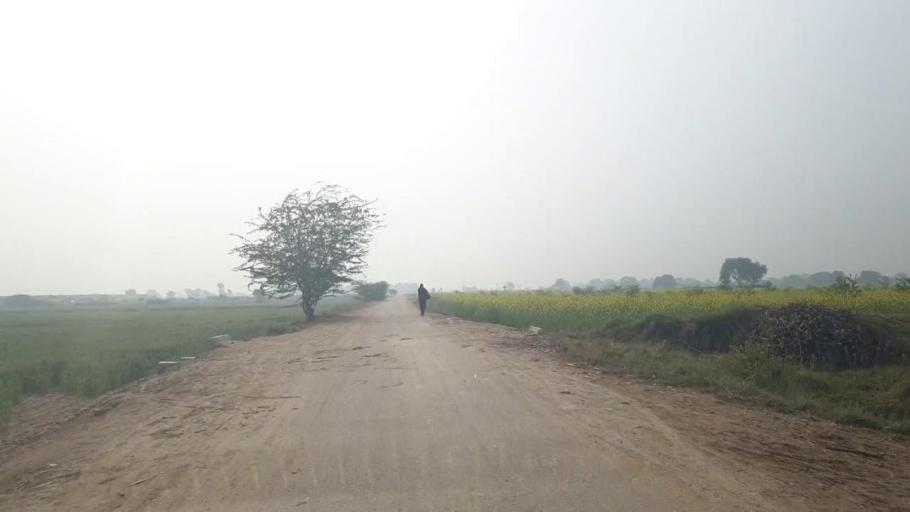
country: PK
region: Sindh
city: Tando Adam
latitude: 25.7102
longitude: 68.6261
